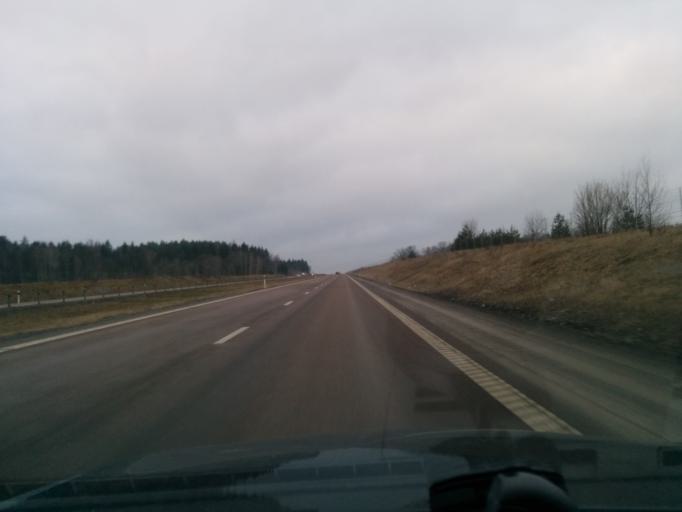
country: SE
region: Uppsala
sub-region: Enkopings Kommun
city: Hummelsta
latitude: 59.6475
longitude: 17.0084
